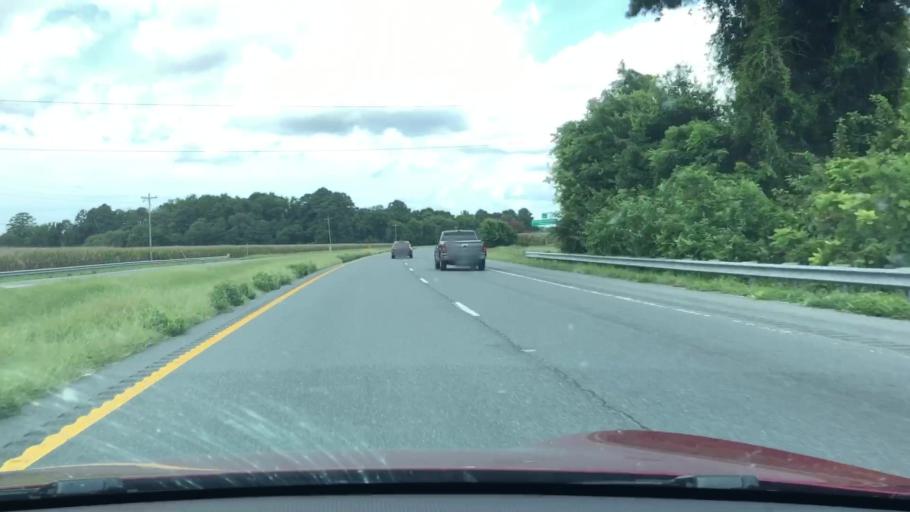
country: US
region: Virginia
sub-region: Northampton County
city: Cape Charles
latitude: 37.2822
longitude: -75.9793
